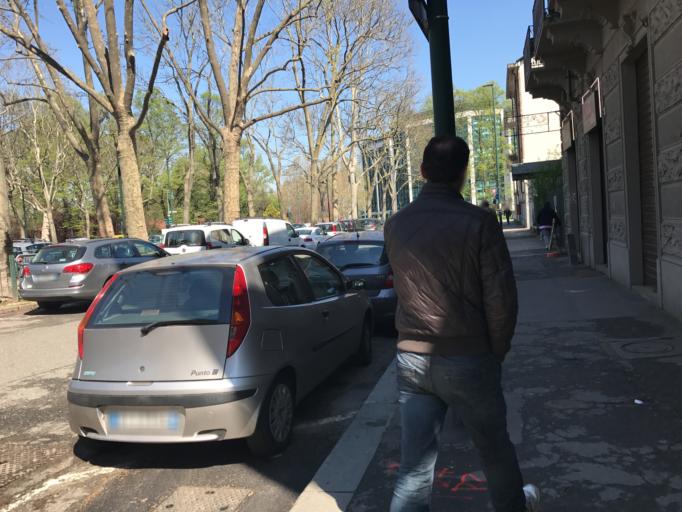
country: IT
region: Piedmont
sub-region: Provincia di Torino
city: Turin
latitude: 45.0740
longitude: 7.7097
